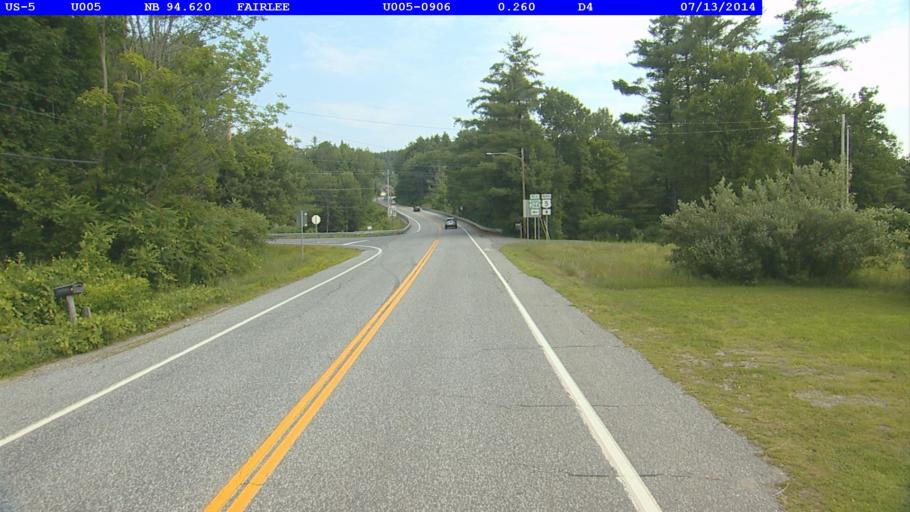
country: US
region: New Hampshire
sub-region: Grafton County
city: Orford
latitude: 43.8780
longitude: -72.1762
